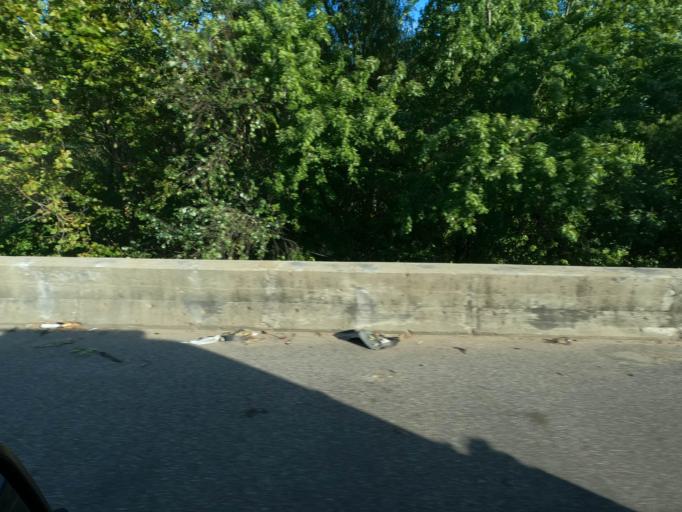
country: US
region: Tennessee
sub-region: Shelby County
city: Memphis
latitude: 35.1875
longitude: -90.0166
